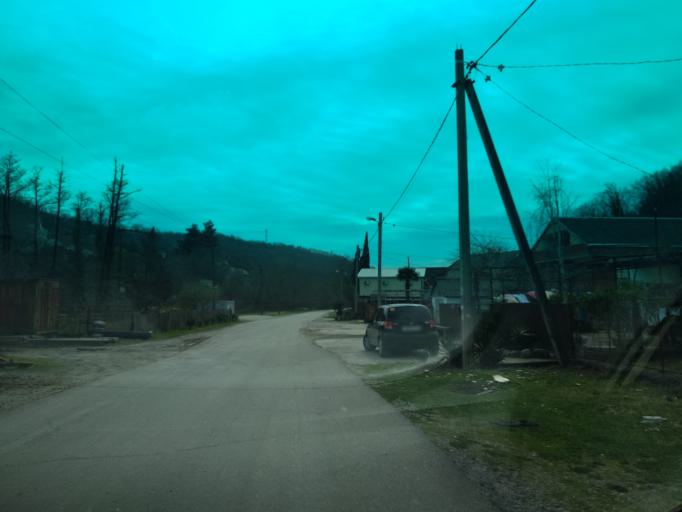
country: RU
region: Krasnodarskiy
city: Shepsi
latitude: 44.0623
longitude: 39.1372
